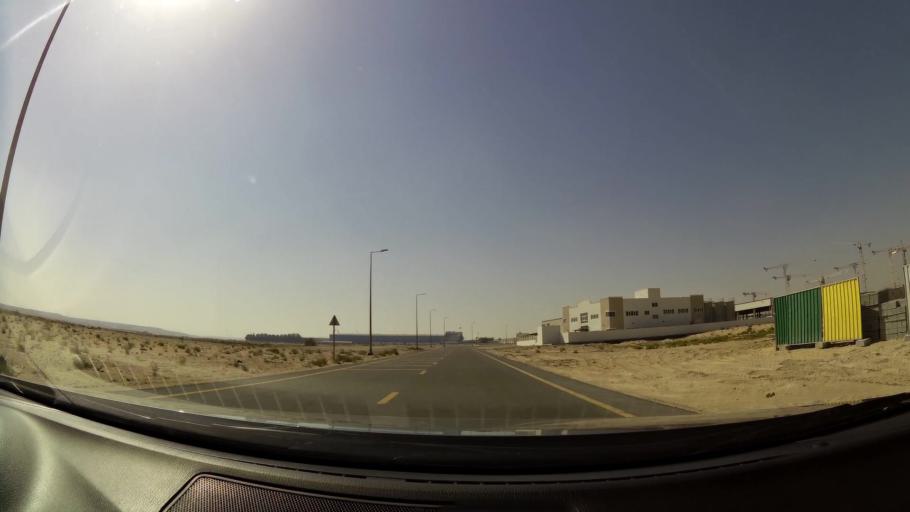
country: AE
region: Dubai
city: Dubai
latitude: 24.9248
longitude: 55.0579
